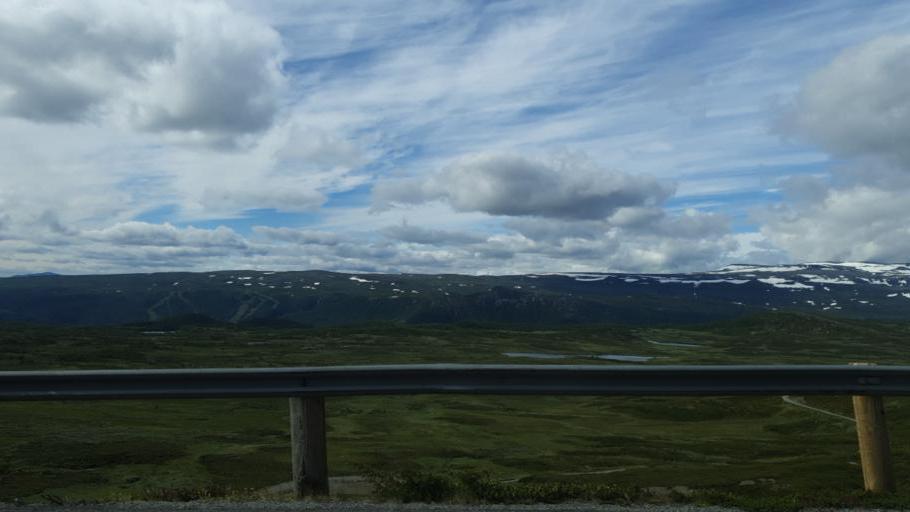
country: NO
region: Oppland
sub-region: Vestre Slidre
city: Slidre
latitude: 61.2798
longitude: 8.8442
